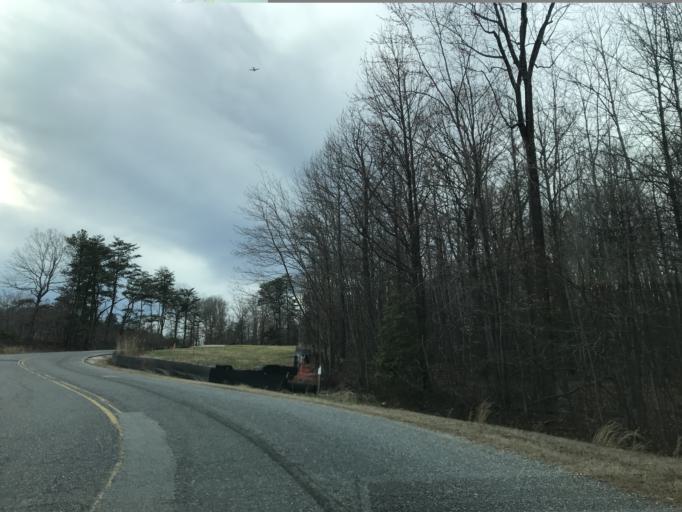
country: US
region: Maryland
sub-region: Howard County
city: Fort George G Mead Junction
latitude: 39.0937
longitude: -76.7844
